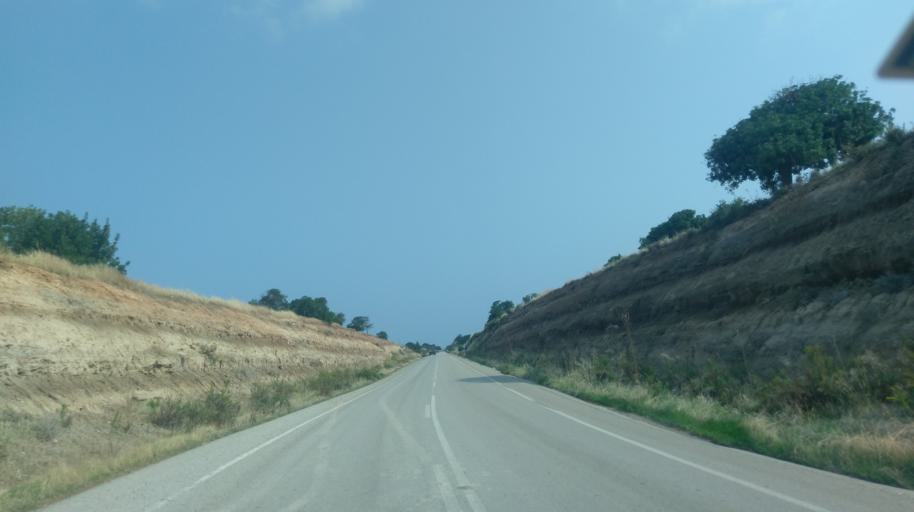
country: CY
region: Ammochostos
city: Lefkonoiko
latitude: 35.4014
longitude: 33.7613
